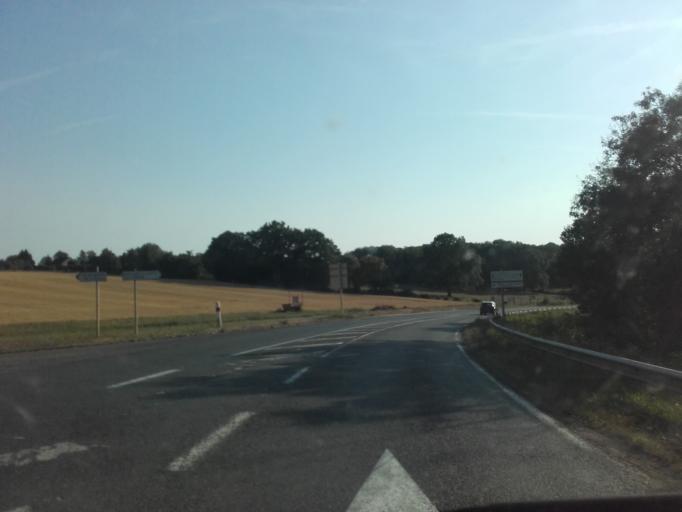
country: FR
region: Bourgogne
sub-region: Departement de l'Yonne
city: Venoy
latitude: 47.7946
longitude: 3.6533
